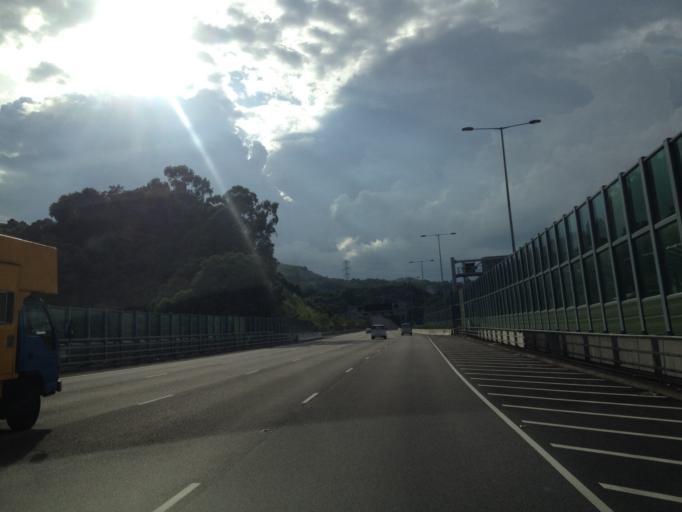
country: HK
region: Tai Po
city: Tai Po
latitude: 22.4392
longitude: 114.1644
